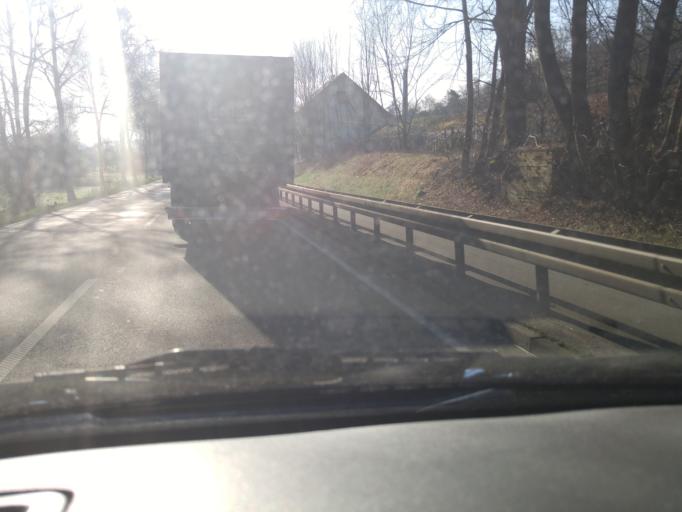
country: DE
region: Hesse
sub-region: Regierungsbezirk Giessen
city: Lauterbach
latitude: 50.6383
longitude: 9.4260
